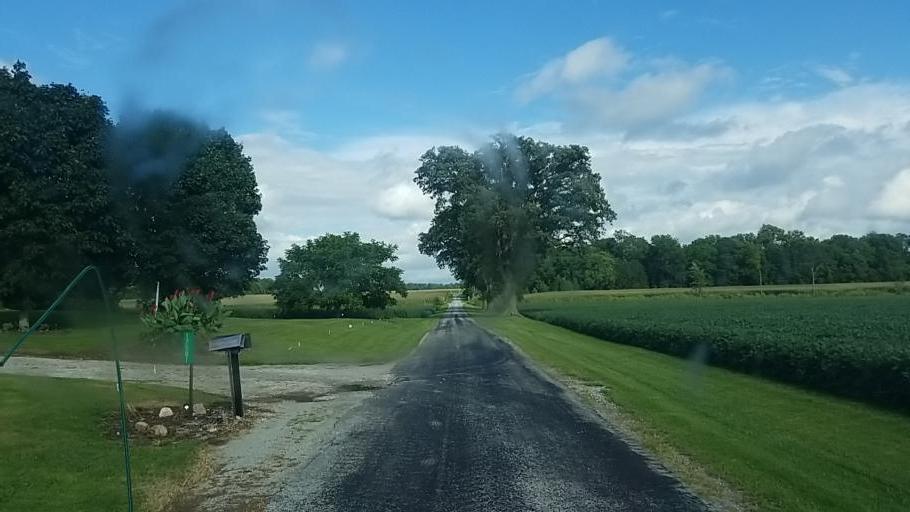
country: US
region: Ohio
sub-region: Hardin County
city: Kenton
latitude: 40.6801
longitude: -83.5463
